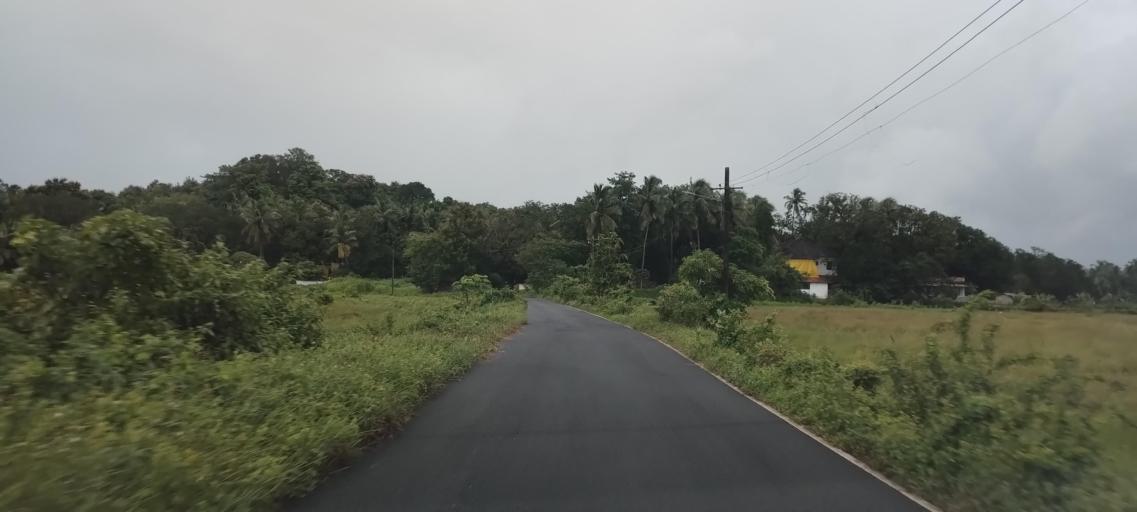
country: IN
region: Goa
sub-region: North Goa
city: Jua
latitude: 15.5190
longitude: 73.8955
